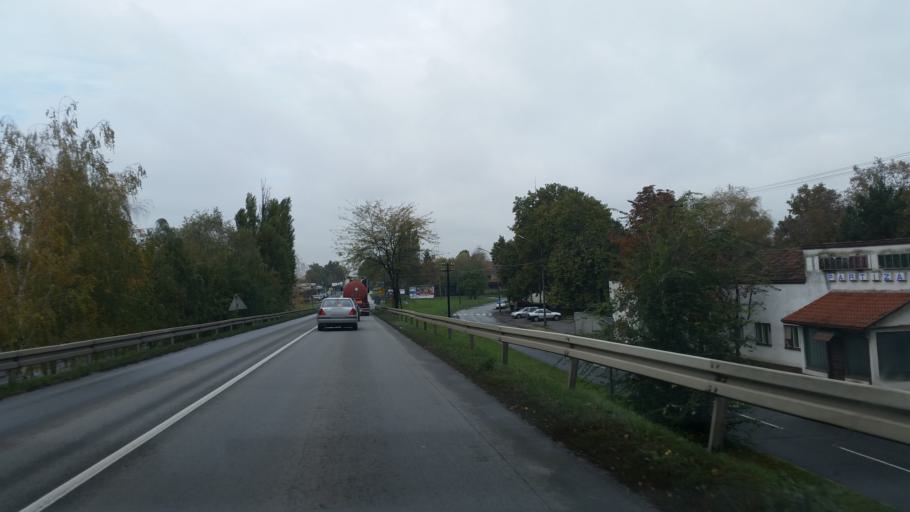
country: RS
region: Autonomna Pokrajina Vojvodina
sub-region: Srednjebanatski Okrug
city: Zrenjanin
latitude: 45.3714
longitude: 20.4177
